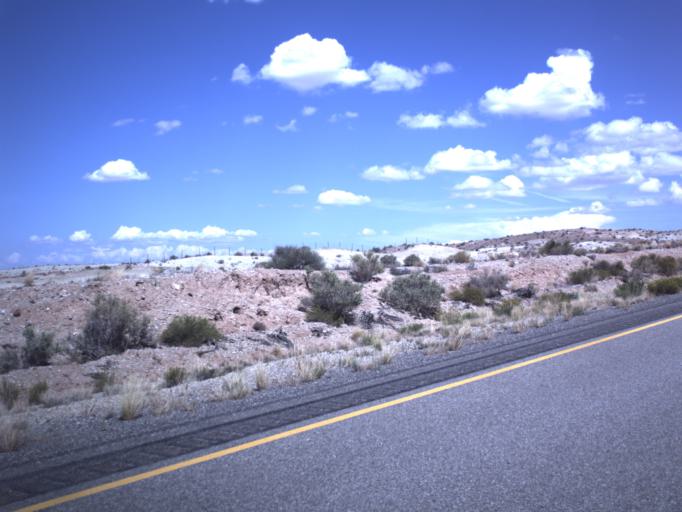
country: US
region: Utah
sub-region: Emery County
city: Ferron
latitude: 38.8474
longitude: -111.0137
